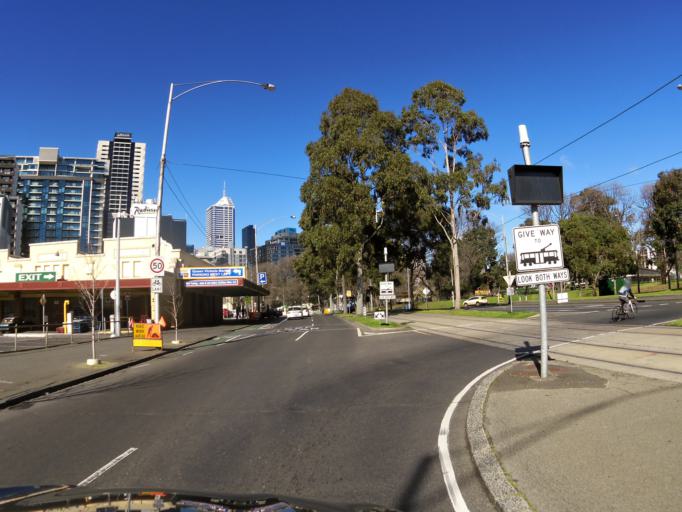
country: AU
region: Victoria
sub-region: Melbourne
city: West Melbourne
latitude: -37.8083
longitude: 144.9556
